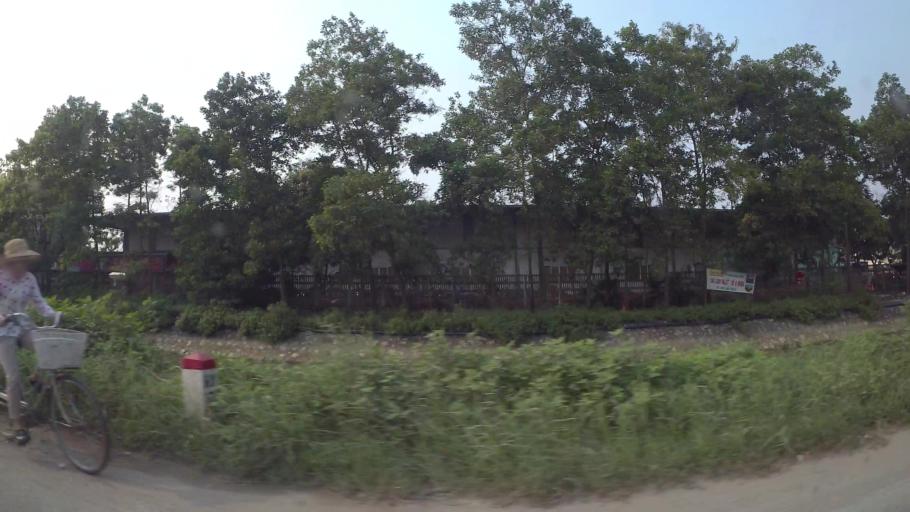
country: VN
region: Ha Noi
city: Thuong Tin
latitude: 20.8714
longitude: 105.8721
